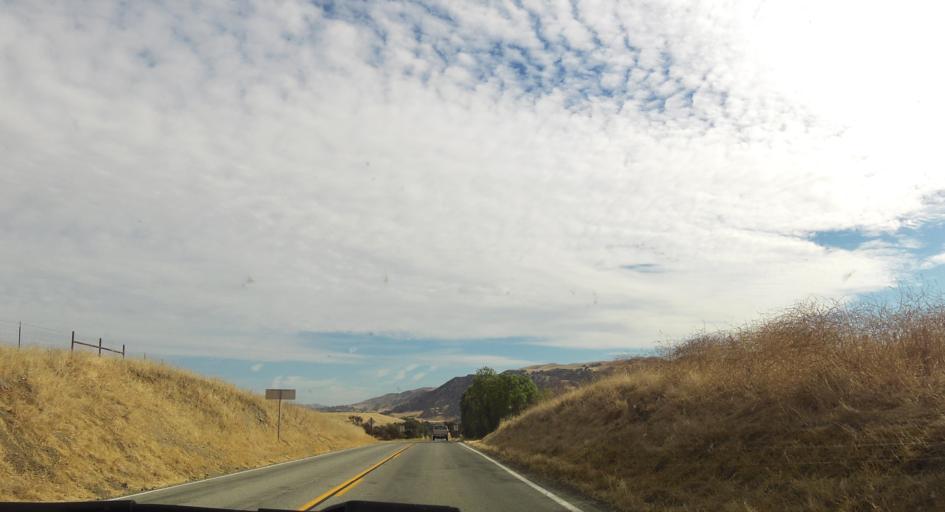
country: US
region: California
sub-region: San Benito County
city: Ridgemark
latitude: 36.7861
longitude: -121.3154
